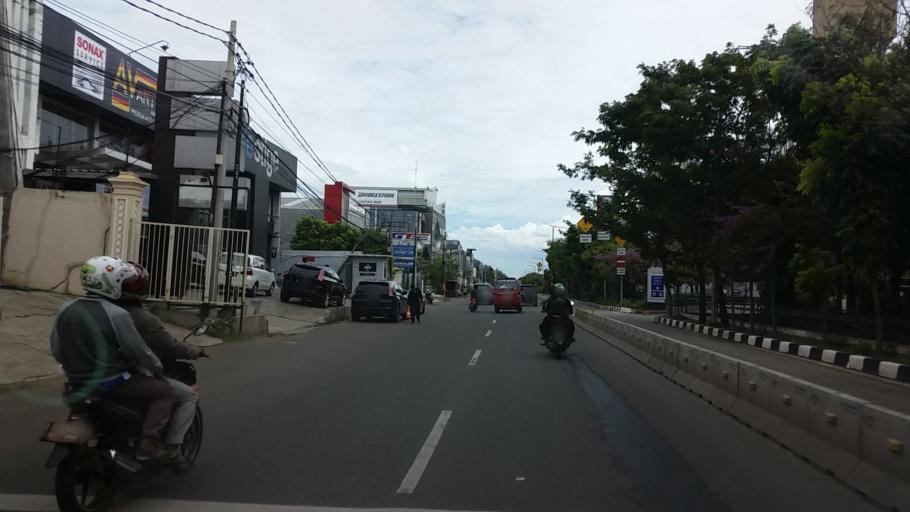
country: ID
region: Jakarta Raya
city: Jakarta
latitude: -6.1158
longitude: 106.7864
